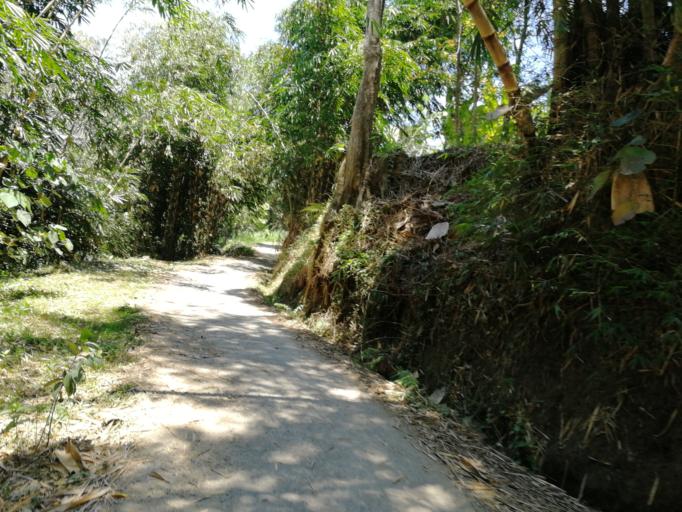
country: ID
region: West Nusa Tenggara
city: Tetebatu
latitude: -8.5473
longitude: 116.4203
